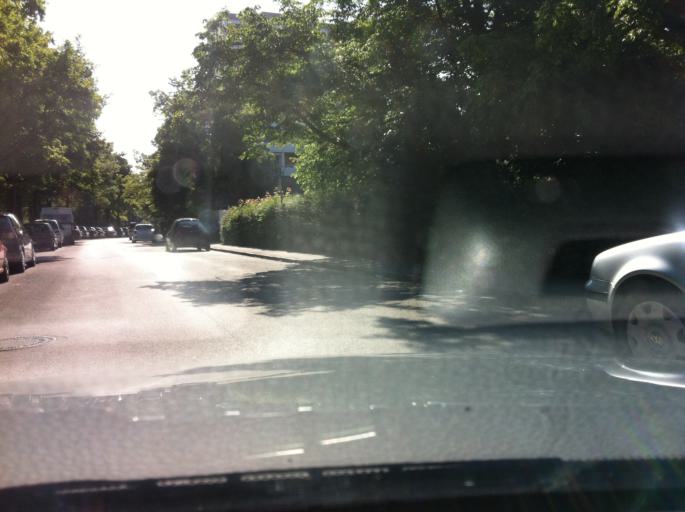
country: DE
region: Bavaria
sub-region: Upper Bavaria
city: Taufkirchen
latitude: 48.0523
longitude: 11.6039
